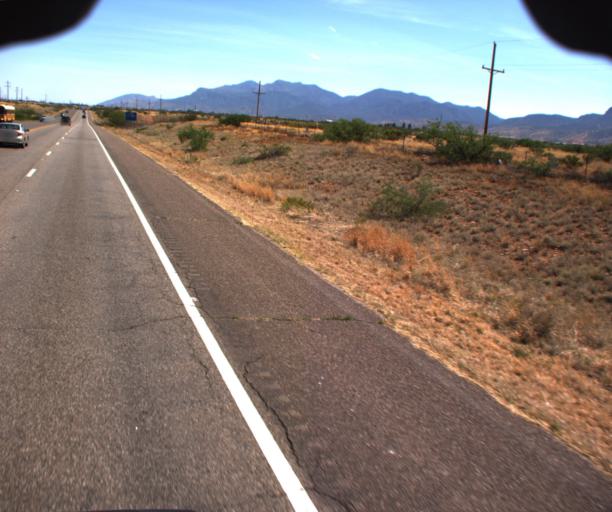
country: US
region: Arizona
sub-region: Cochise County
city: Sierra Vista
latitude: 31.5830
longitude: -110.3195
